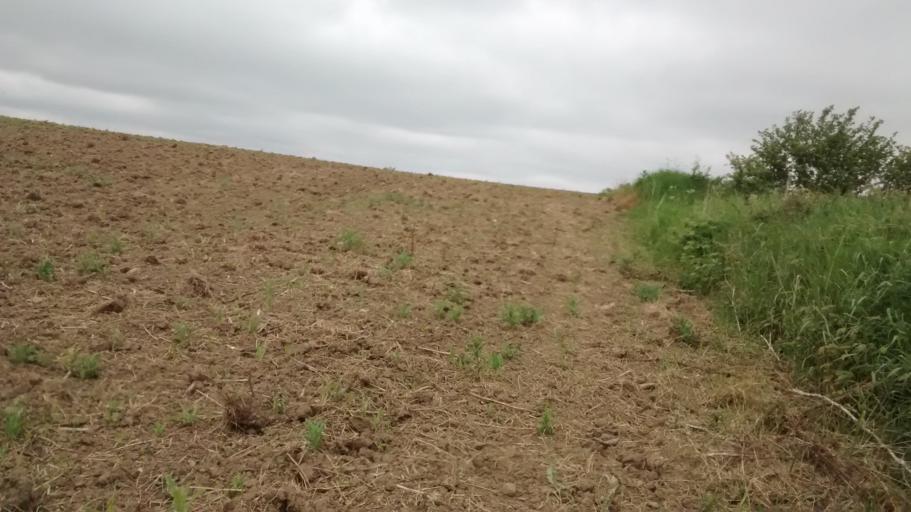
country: GB
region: England
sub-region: County Durham
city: Pittington
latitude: 54.7956
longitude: -1.4818
